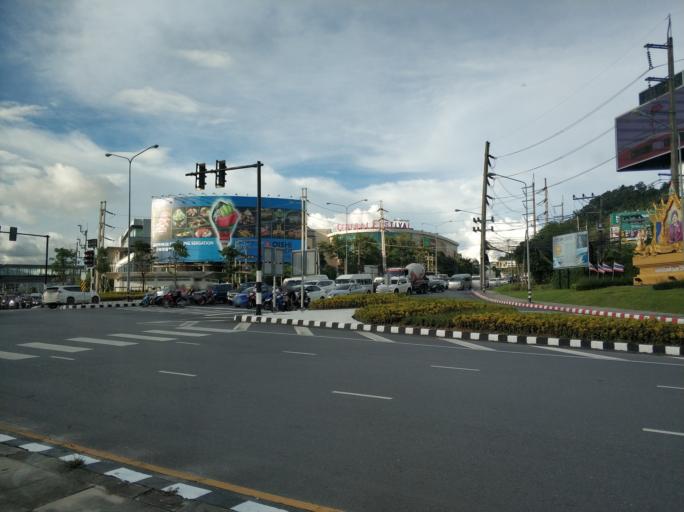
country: TH
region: Phuket
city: Wichit
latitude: 7.8893
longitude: 98.3681
